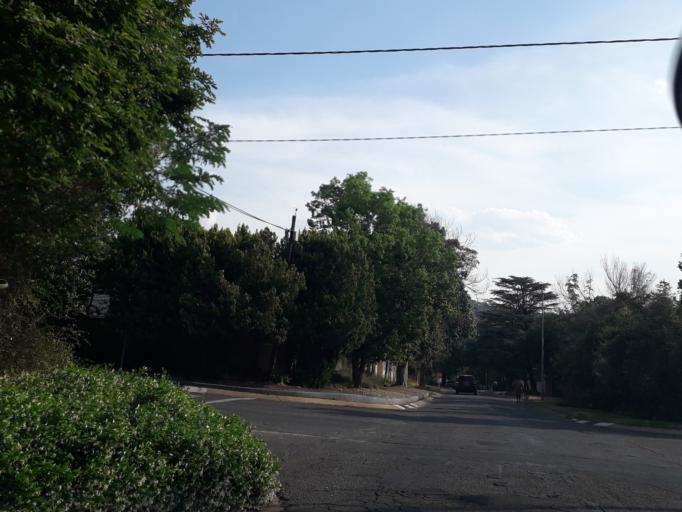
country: ZA
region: Gauteng
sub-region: City of Johannesburg Metropolitan Municipality
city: Johannesburg
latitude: -26.0991
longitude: 28.0425
